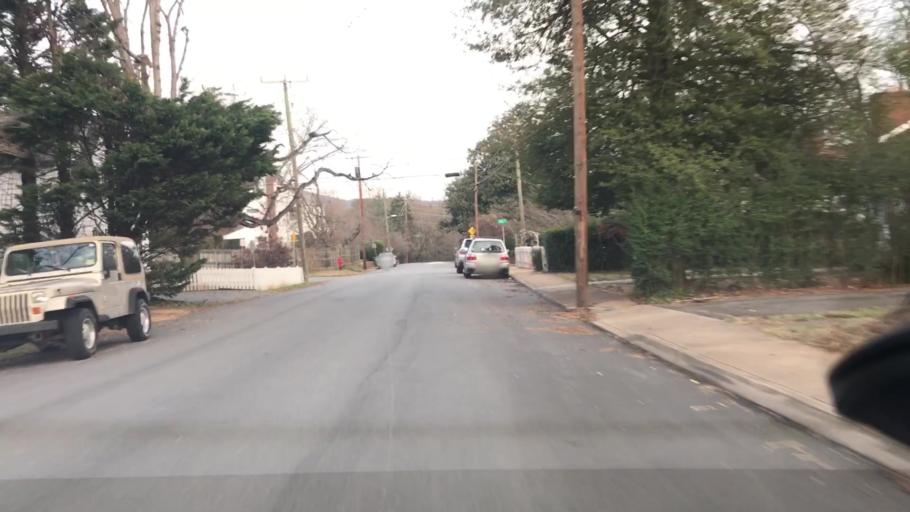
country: US
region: Virginia
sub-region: City of Charlottesville
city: Charlottesville
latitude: 38.0244
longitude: -78.5124
